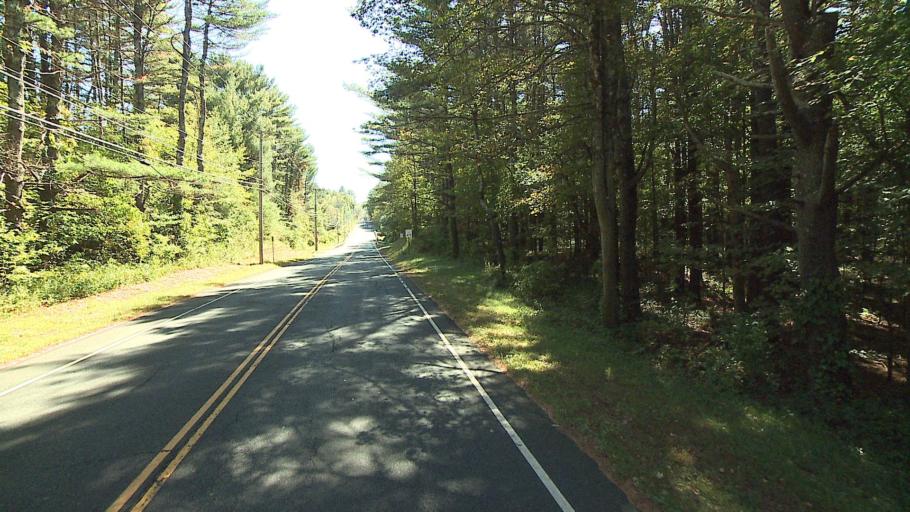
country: US
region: Connecticut
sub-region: Litchfield County
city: New Hartford Center
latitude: 41.8275
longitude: -72.9763
